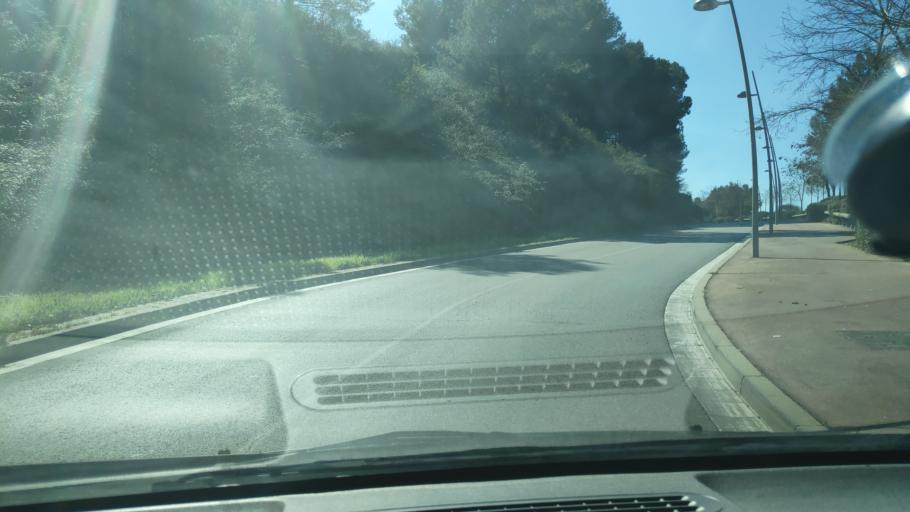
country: ES
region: Catalonia
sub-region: Provincia de Barcelona
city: Rubi
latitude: 41.5078
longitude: 2.0458
